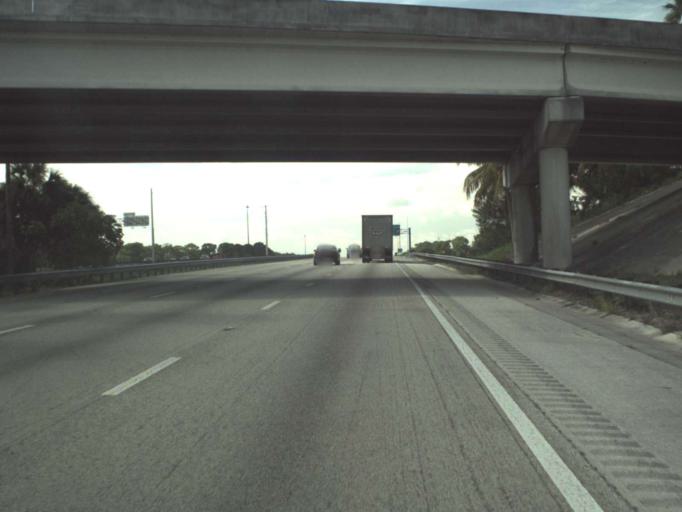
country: US
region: Florida
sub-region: Palm Beach County
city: Limestone Creek
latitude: 26.9368
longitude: -80.1510
